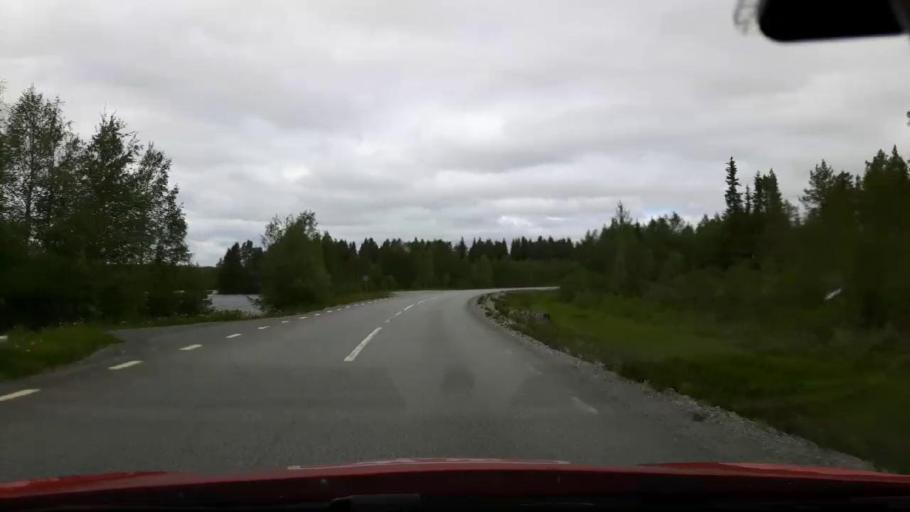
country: SE
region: Jaemtland
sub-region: OEstersunds Kommun
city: Lit
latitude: 63.6831
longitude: 14.6739
